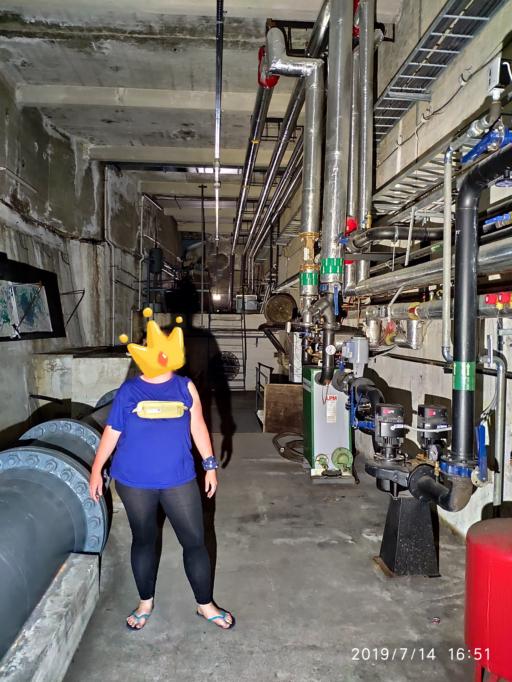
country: NO
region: Hordaland
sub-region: Odda
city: Odda
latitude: 60.1213
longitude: 6.5563
